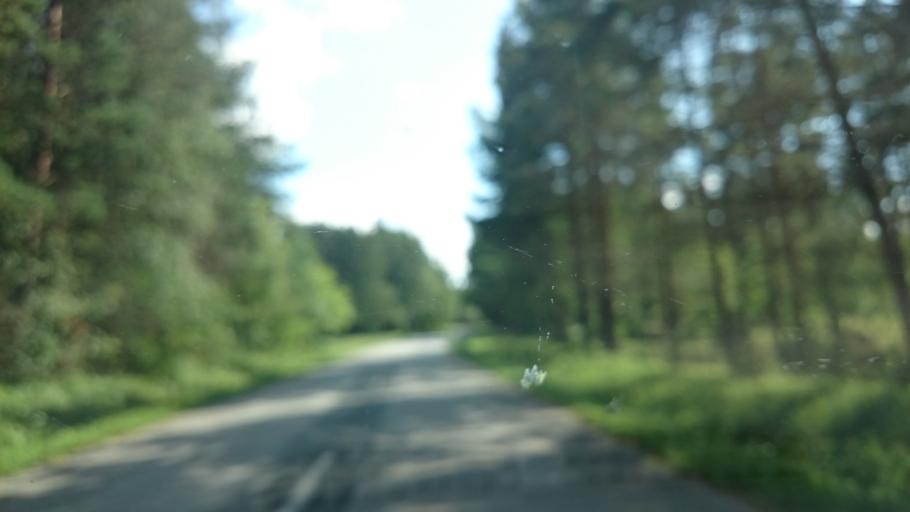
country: EE
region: Saare
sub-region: Orissaare vald
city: Orissaare
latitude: 58.5825
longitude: 22.7656
